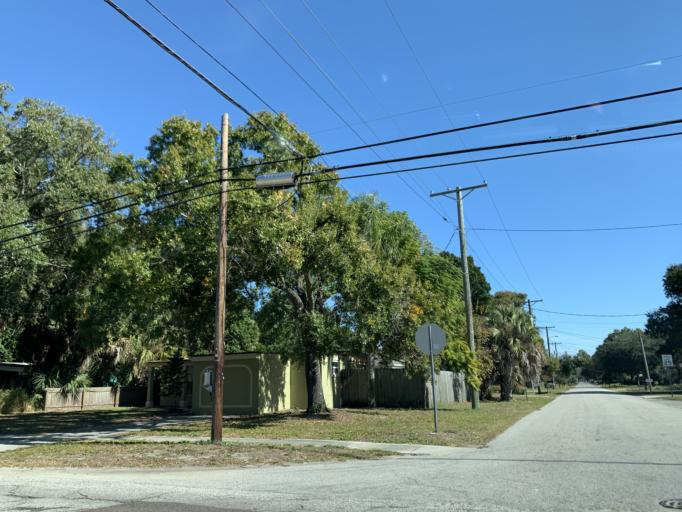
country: US
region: Florida
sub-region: Hillsborough County
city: Tampa
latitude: 27.8892
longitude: -82.5022
